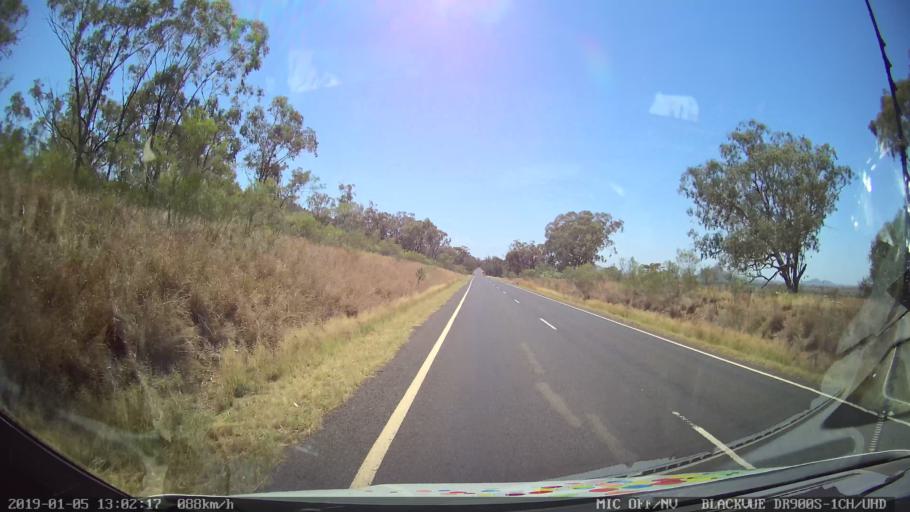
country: AU
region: New South Wales
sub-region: Narrabri
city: Boggabri
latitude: -31.1157
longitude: 149.8094
